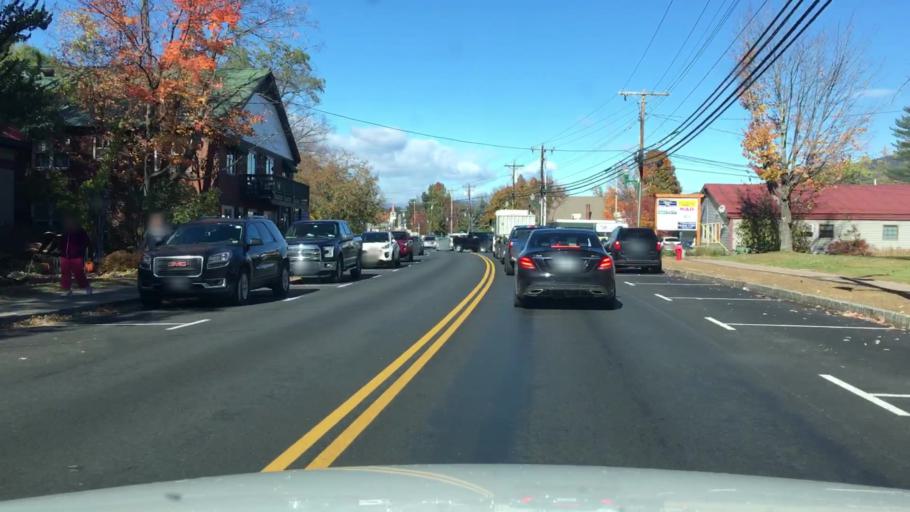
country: US
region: New Hampshire
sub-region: Carroll County
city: North Conway
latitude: 44.0487
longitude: -71.1248
